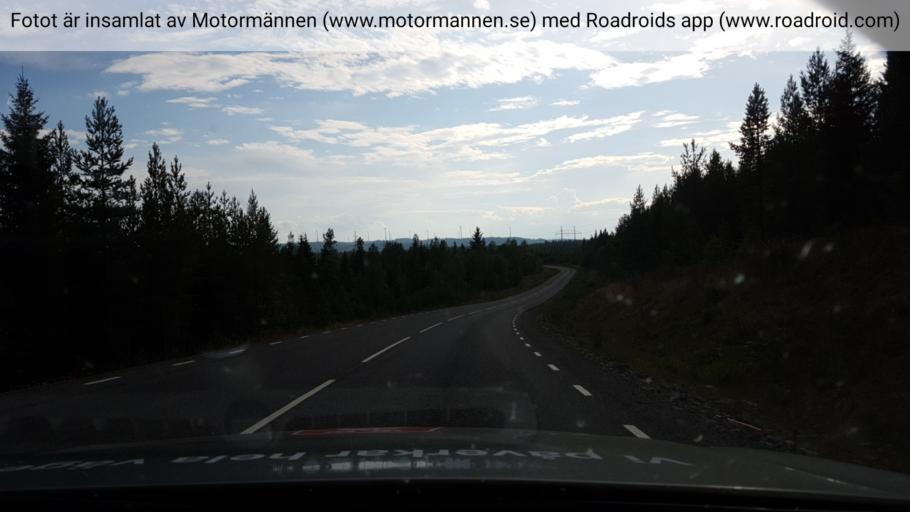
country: SE
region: Jaemtland
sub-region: Ragunda Kommun
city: Hammarstrand
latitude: 63.5471
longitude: 16.0972
